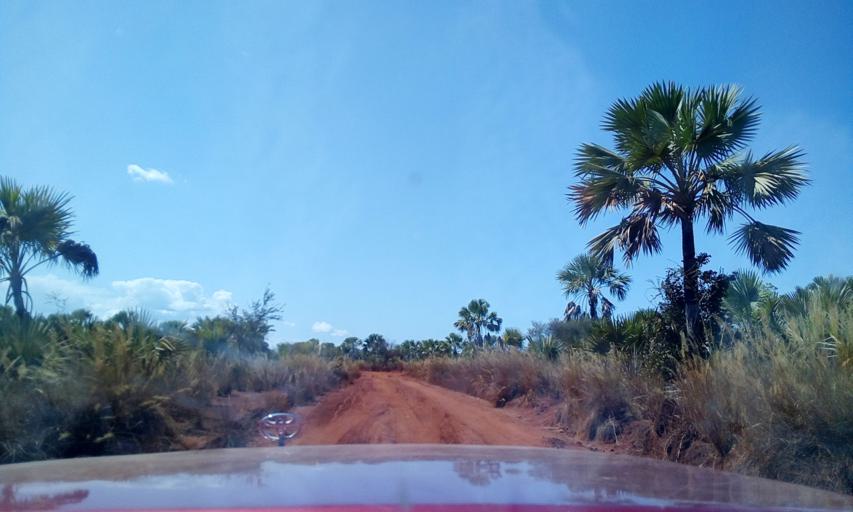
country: MG
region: Boeny
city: Sitampiky
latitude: -16.1280
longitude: 45.4429
